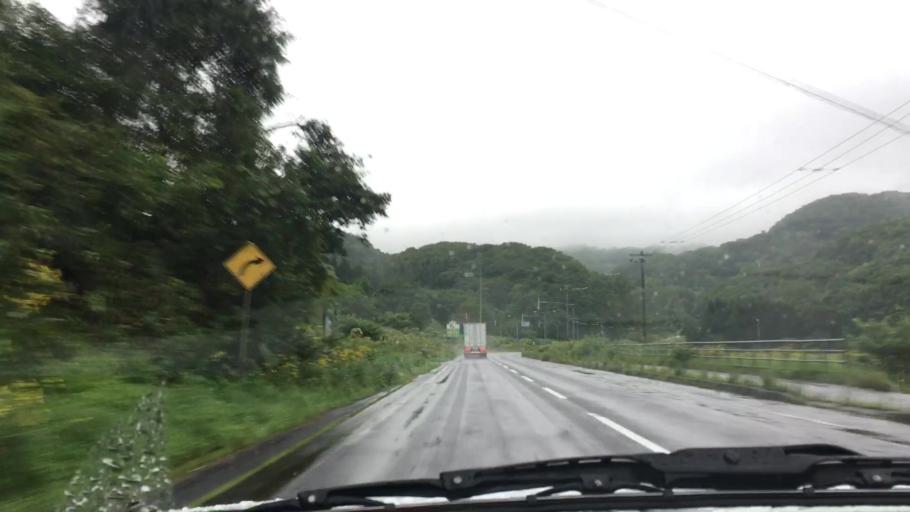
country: JP
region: Hokkaido
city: Niseko Town
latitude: 42.6006
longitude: 140.6243
